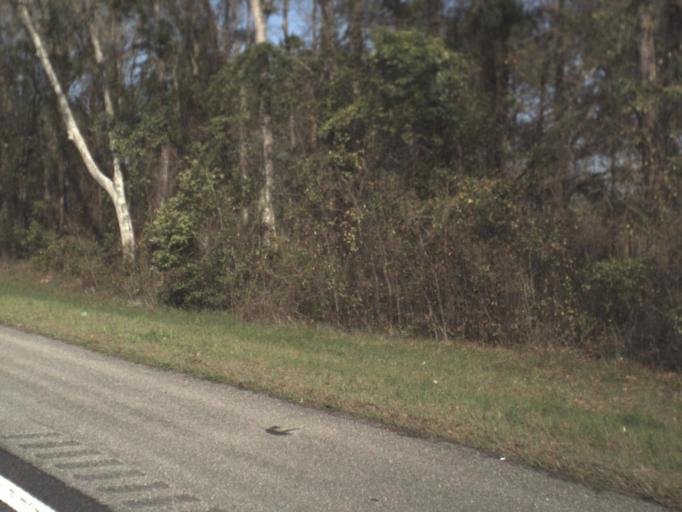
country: US
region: Florida
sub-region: Leon County
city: Tallahassee
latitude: 30.4783
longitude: -84.1092
